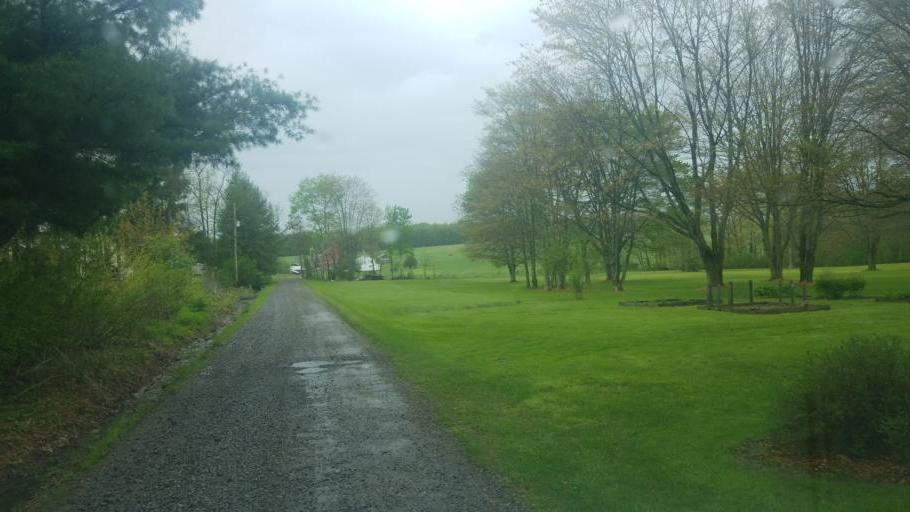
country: US
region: Pennsylvania
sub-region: Forest County
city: Tionesta
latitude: 41.3965
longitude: -79.3887
